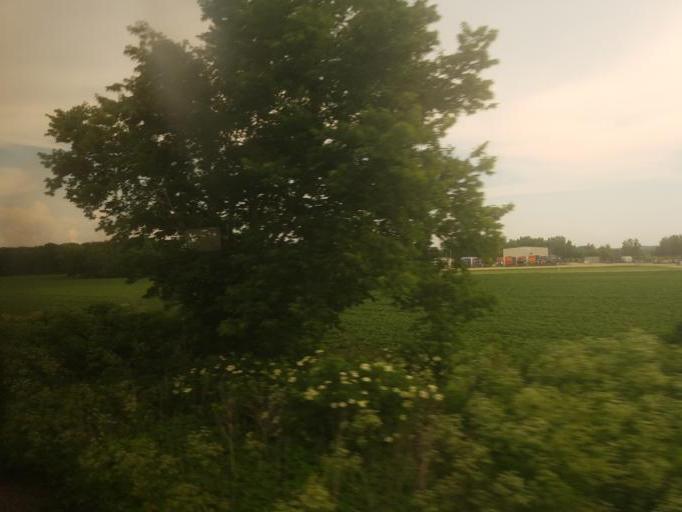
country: US
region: Illinois
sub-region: Bureau County
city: Princeton
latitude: 41.3912
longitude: -89.4916
